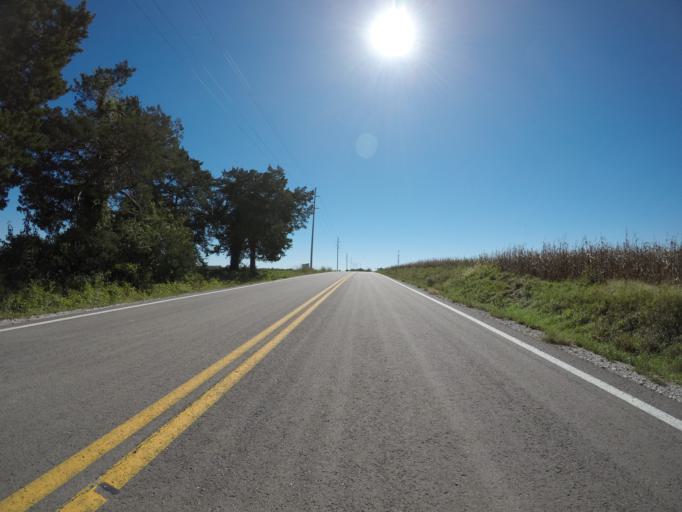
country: US
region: Kansas
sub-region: Johnson County
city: De Soto
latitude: 38.9486
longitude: -95.0195
